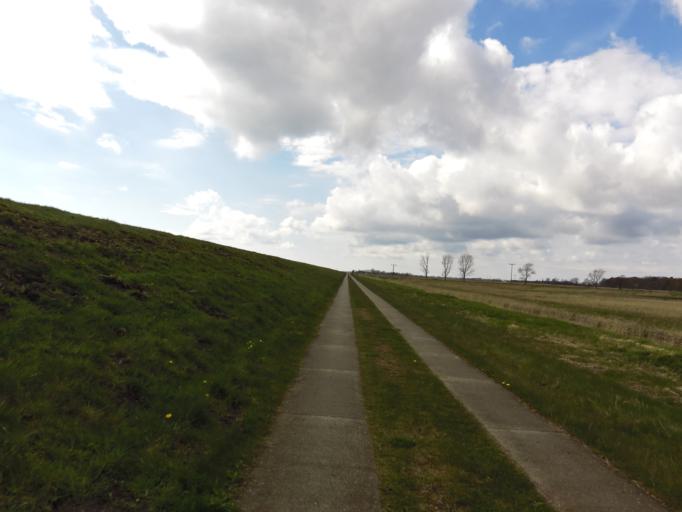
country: DE
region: Mecklenburg-Vorpommern
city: Barth
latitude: 54.4146
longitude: 12.7572
